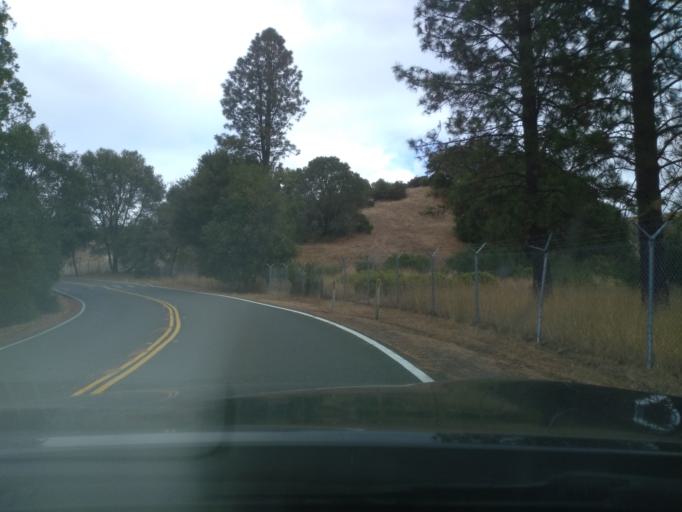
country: US
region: California
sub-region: Mendocino County
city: Ukiah
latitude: 39.1996
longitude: -123.1857
